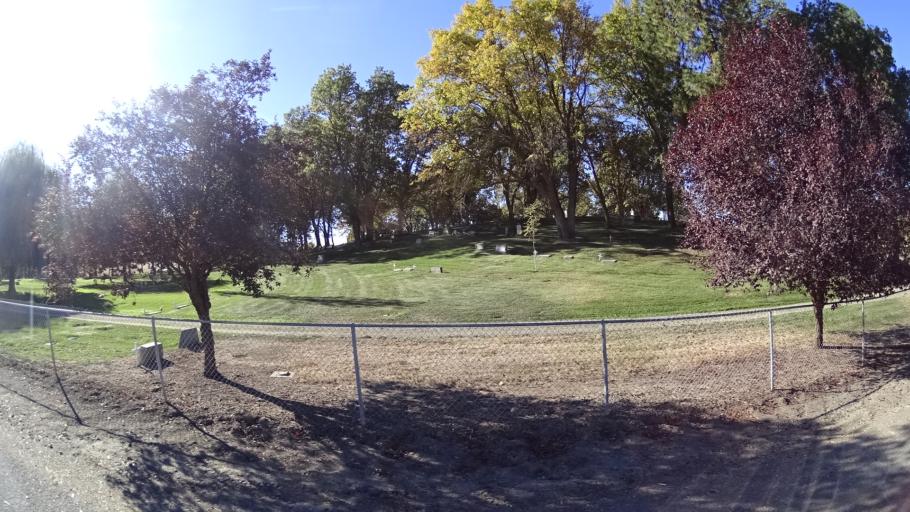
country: US
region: California
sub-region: Siskiyou County
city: Yreka
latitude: 41.5910
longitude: -122.8348
